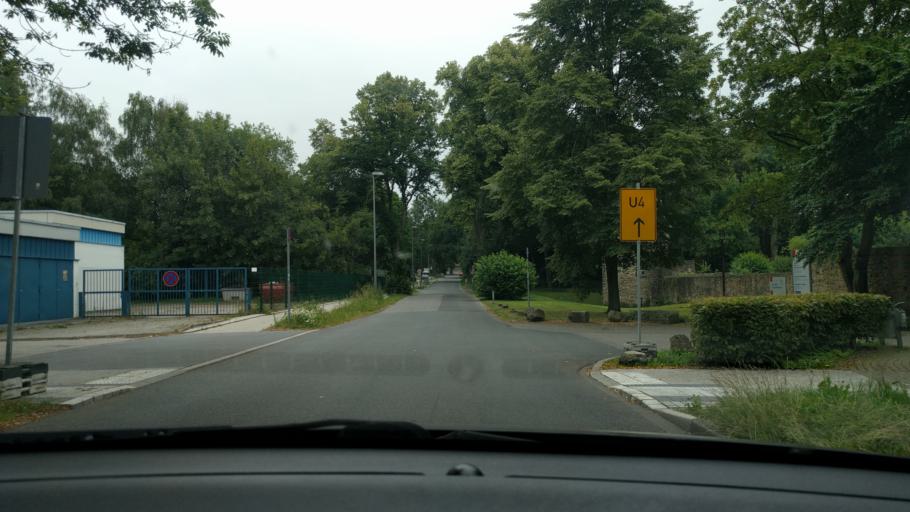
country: DE
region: North Rhine-Westphalia
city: Witten
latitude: 51.4774
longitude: 7.3264
